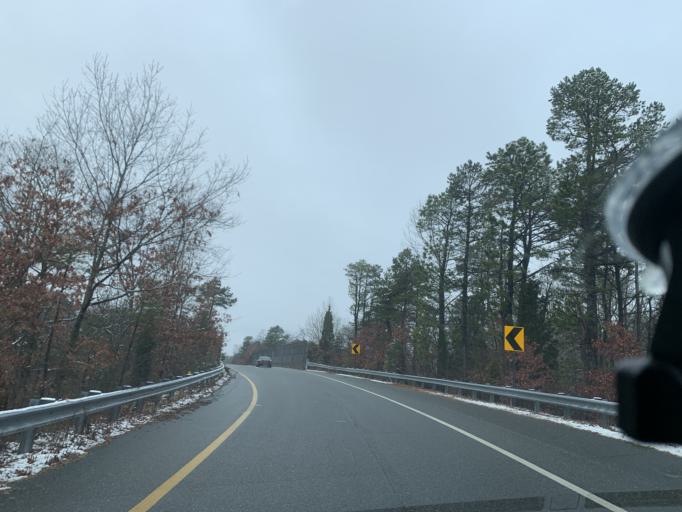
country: US
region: New Jersey
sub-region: Atlantic County
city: Pomona
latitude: 39.4497
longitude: -74.6233
